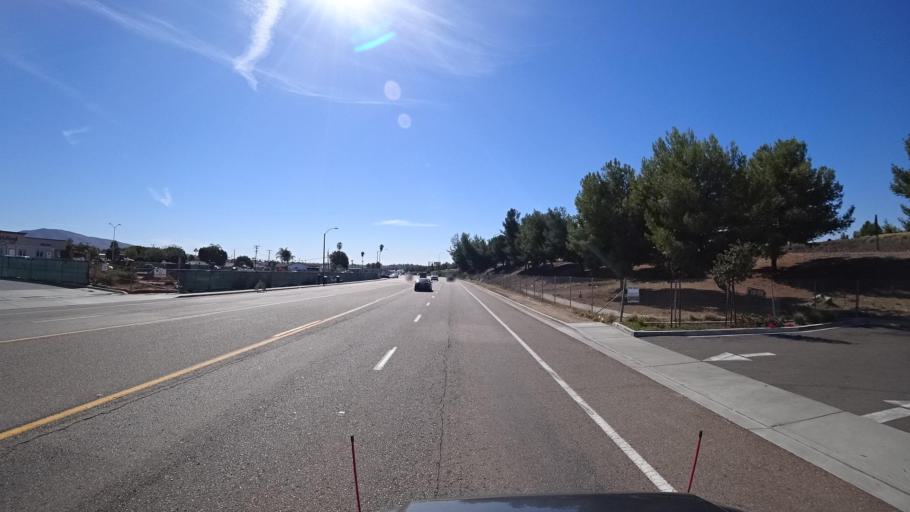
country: US
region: California
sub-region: San Diego County
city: La Presa
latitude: 32.7133
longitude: -117.0128
